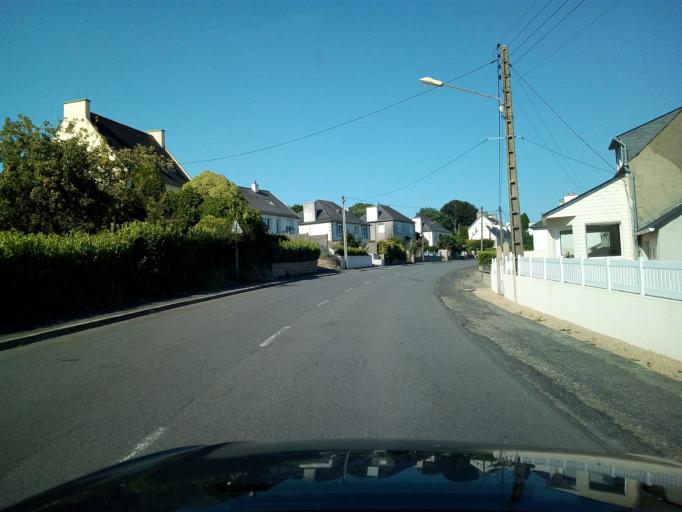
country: FR
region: Brittany
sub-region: Departement du Finistere
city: Landivisiau
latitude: 48.4989
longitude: -4.0753
